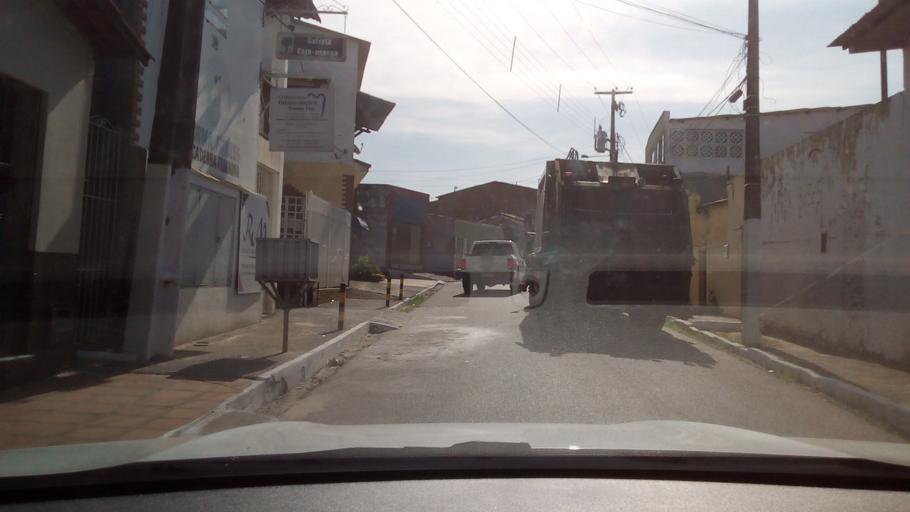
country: BR
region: Rio Grande do Norte
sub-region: Goianinha
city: Goianinha
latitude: -6.2667
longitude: -35.2064
